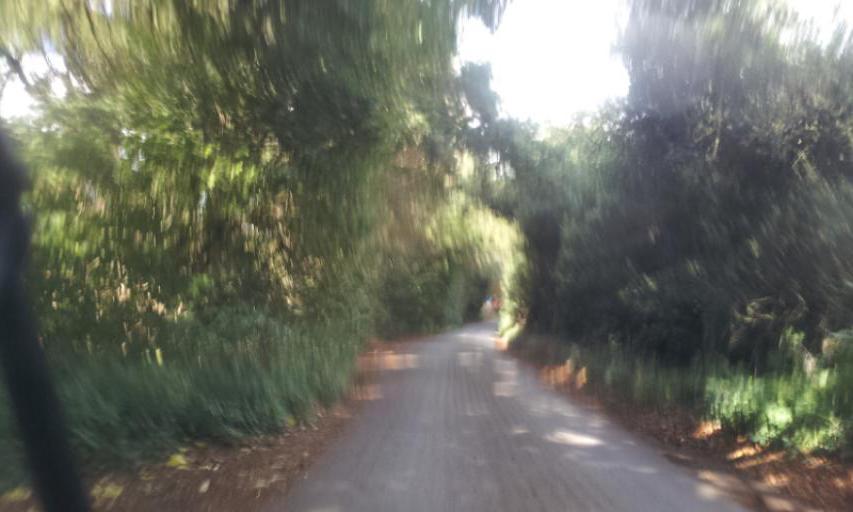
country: GB
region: England
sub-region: Kent
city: West Malling
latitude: 51.3070
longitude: 0.4150
